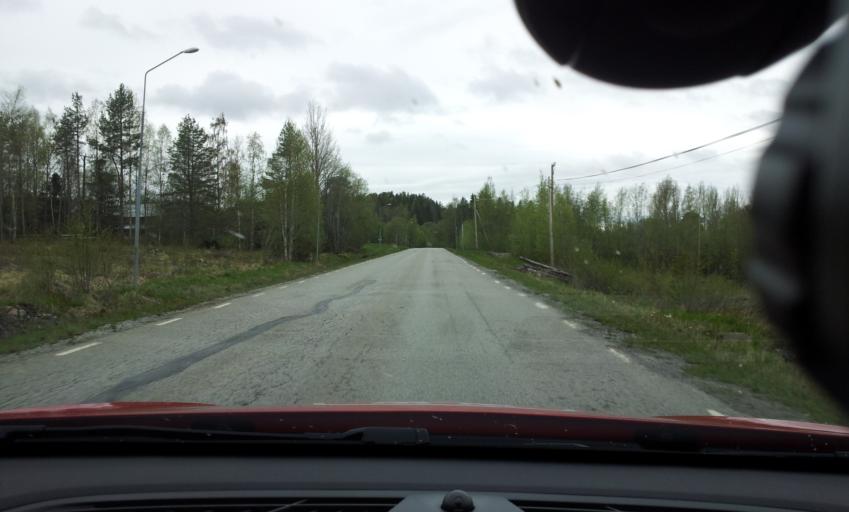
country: SE
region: Jaemtland
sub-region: Bergs Kommun
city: Hoverberg
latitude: 62.7661
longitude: 14.5533
